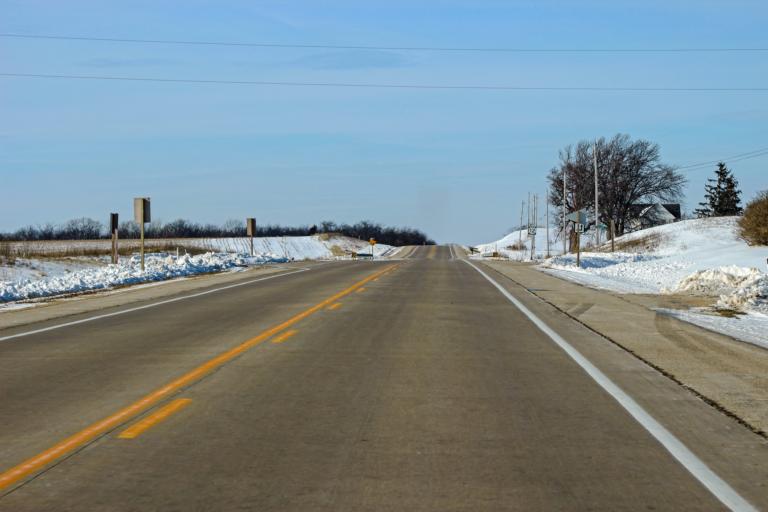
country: US
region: Wisconsin
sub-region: Jefferson County
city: Lake Ripley
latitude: 42.9796
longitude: -88.9627
